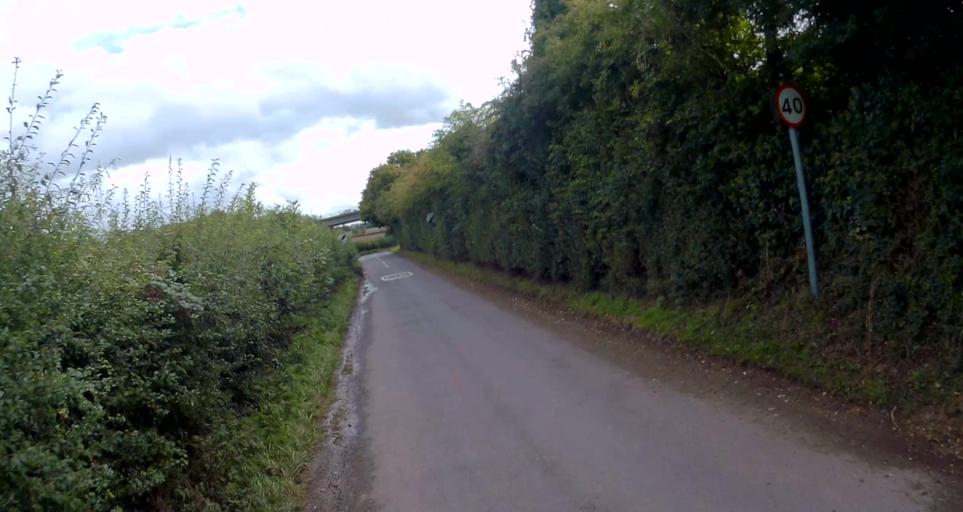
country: GB
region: England
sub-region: Hampshire
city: Kings Worthy
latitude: 51.0826
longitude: -1.1830
